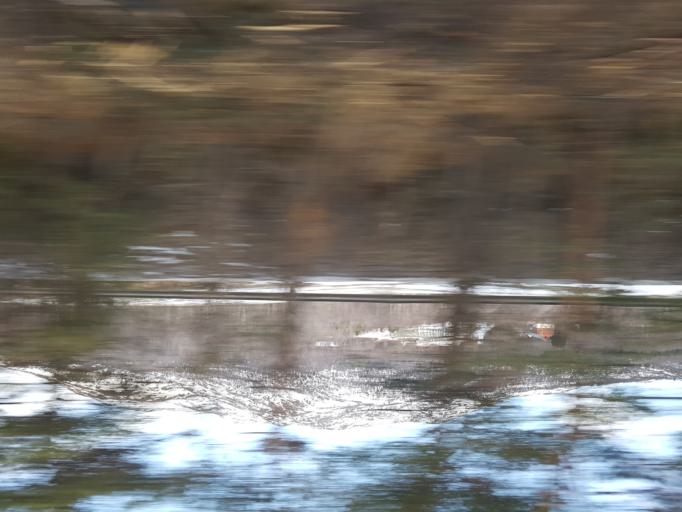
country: NO
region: Sor-Trondelag
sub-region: Oppdal
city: Oppdal
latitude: 62.6174
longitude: 9.7572
